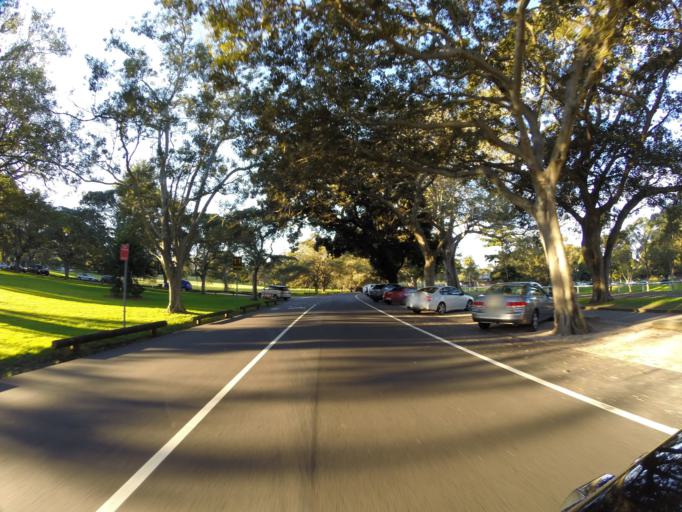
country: AU
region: New South Wales
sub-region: Woollahra
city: Woollahra
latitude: -33.8953
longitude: 151.2315
